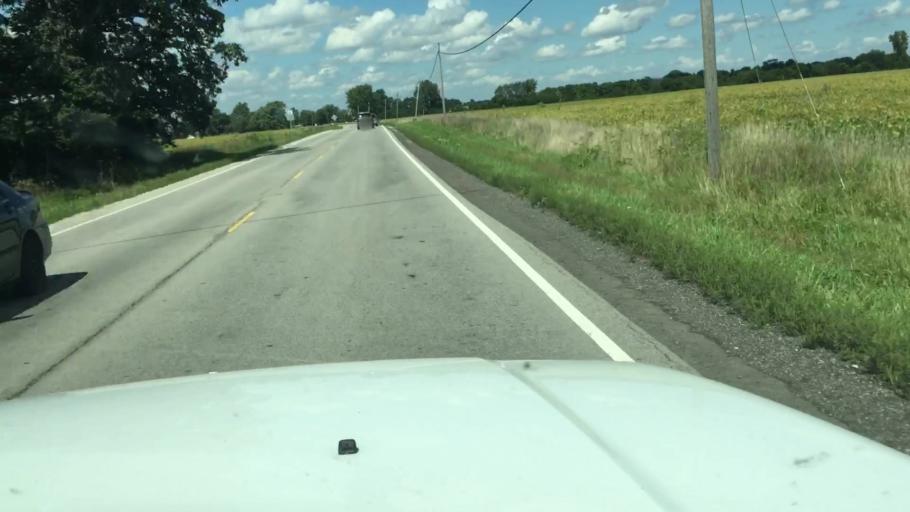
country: US
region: Ohio
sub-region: Madison County
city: Mount Sterling
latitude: 39.7321
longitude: -83.2721
